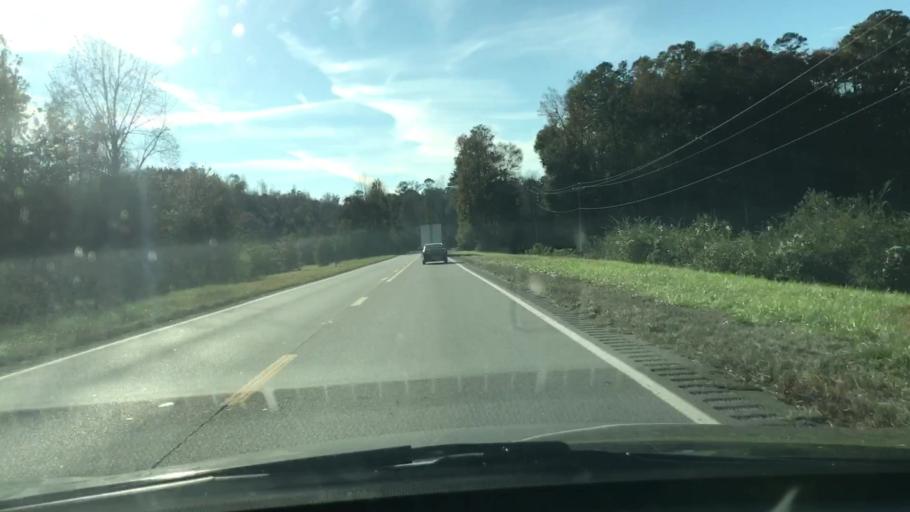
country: US
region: Alabama
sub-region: Cleburne County
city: Heflin
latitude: 33.6397
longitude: -85.6068
